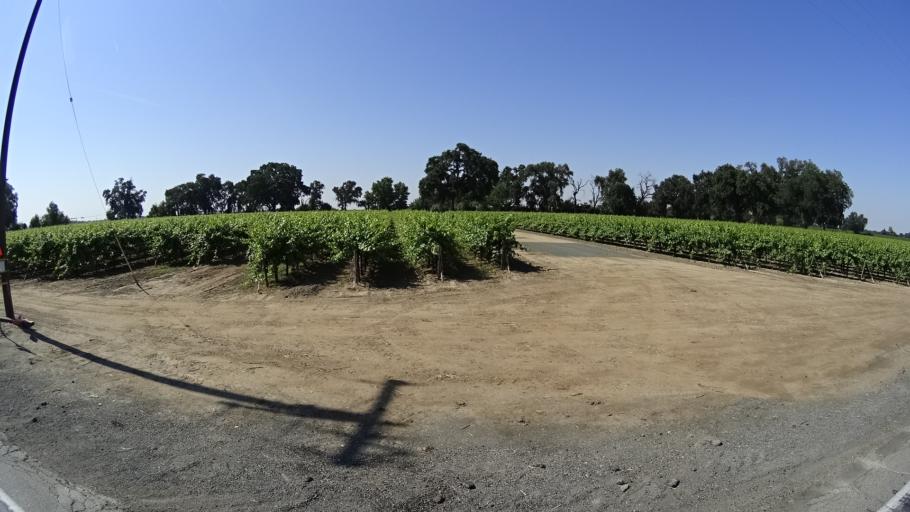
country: US
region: California
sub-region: Kings County
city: Lemoore
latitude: 36.3441
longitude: -119.8251
